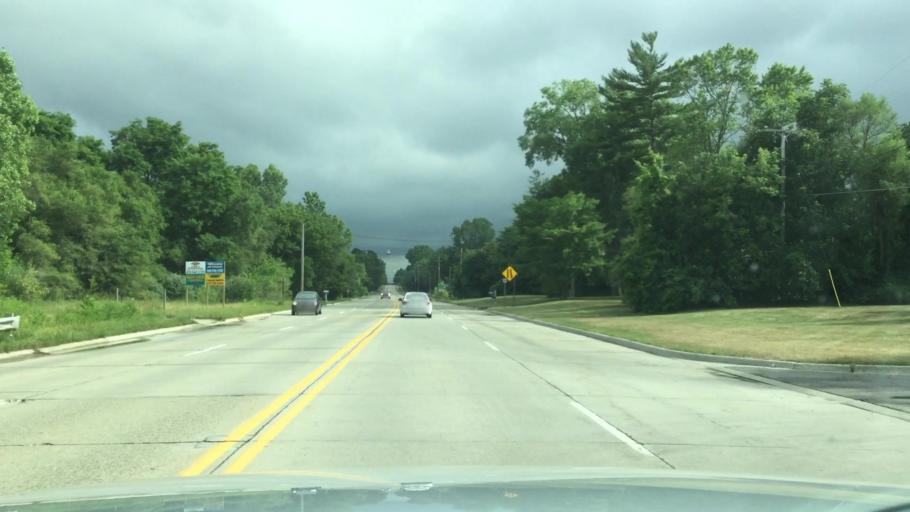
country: US
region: Michigan
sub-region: Genesee County
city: Burton
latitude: 43.0495
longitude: -83.6160
